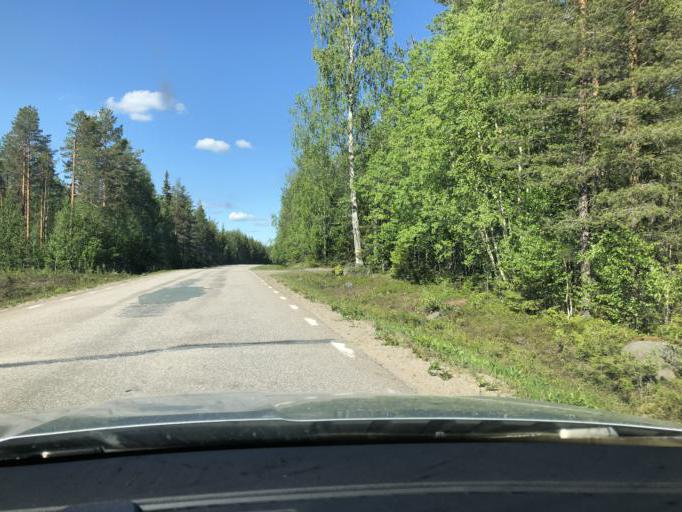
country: SE
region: Norrbotten
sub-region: Kalix Kommun
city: Kalix
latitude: 65.8897
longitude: 23.1544
